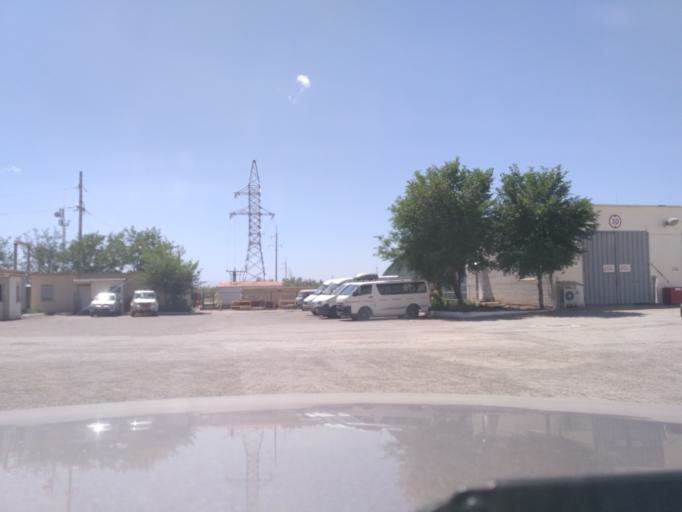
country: KZ
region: Ongtustik Qazaqstan
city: Sholaqqkorghan
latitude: 44.2399
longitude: 68.9236
